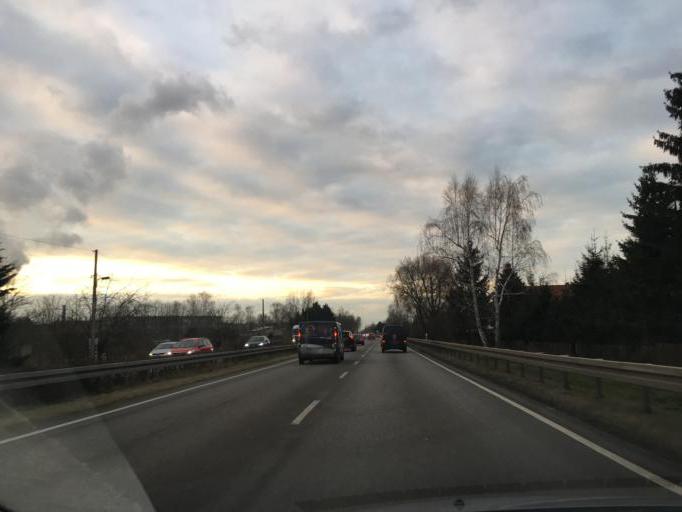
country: DE
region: Saxony
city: Espenhain
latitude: 51.1895
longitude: 12.4741
